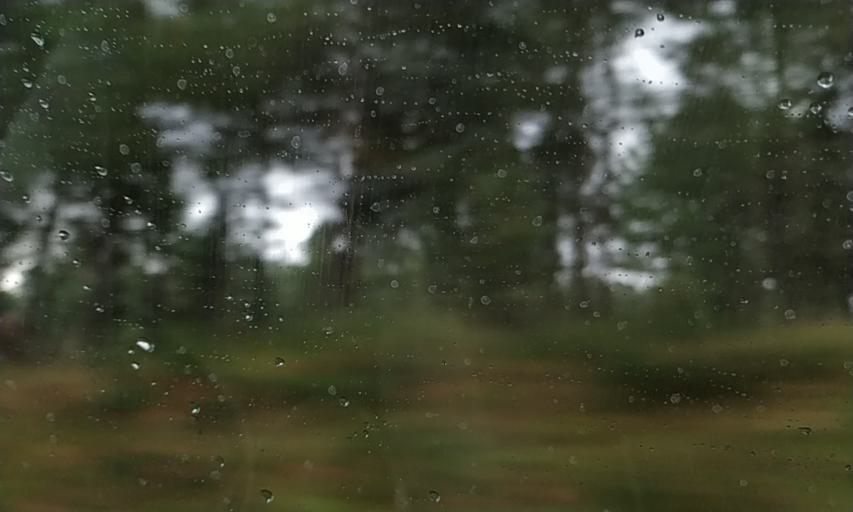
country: PT
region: Vila Real
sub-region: Murca
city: Murca
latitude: 41.3865
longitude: -7.4978
